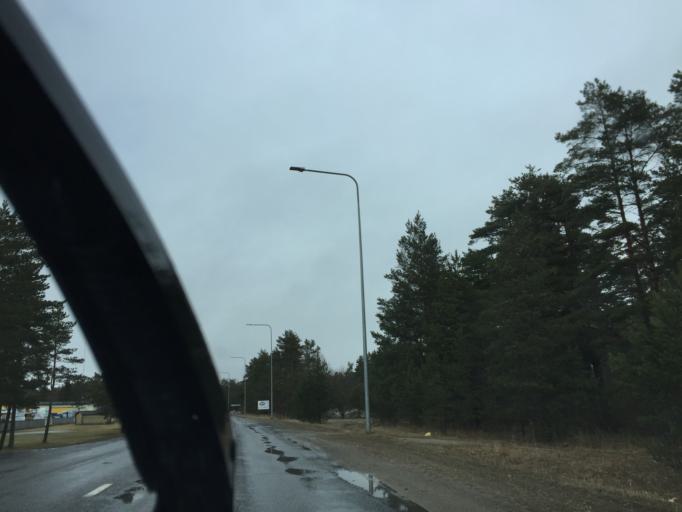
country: EE
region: Laeaene
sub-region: Haapsalu linn
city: Haapsalu
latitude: 58.9197
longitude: 23.5491
